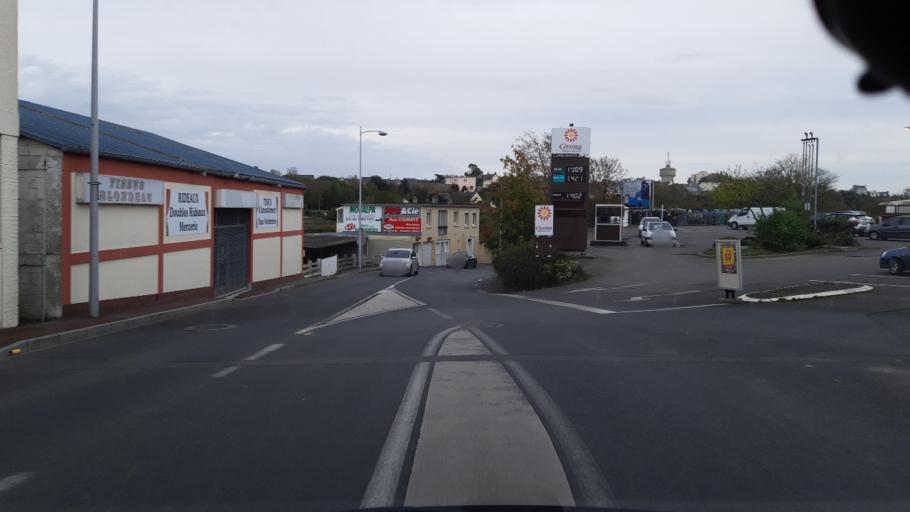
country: FR
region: Lower Normandy
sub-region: Departement de la Manche
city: Donville-les-Bains
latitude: 48.8448
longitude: -1.5837
